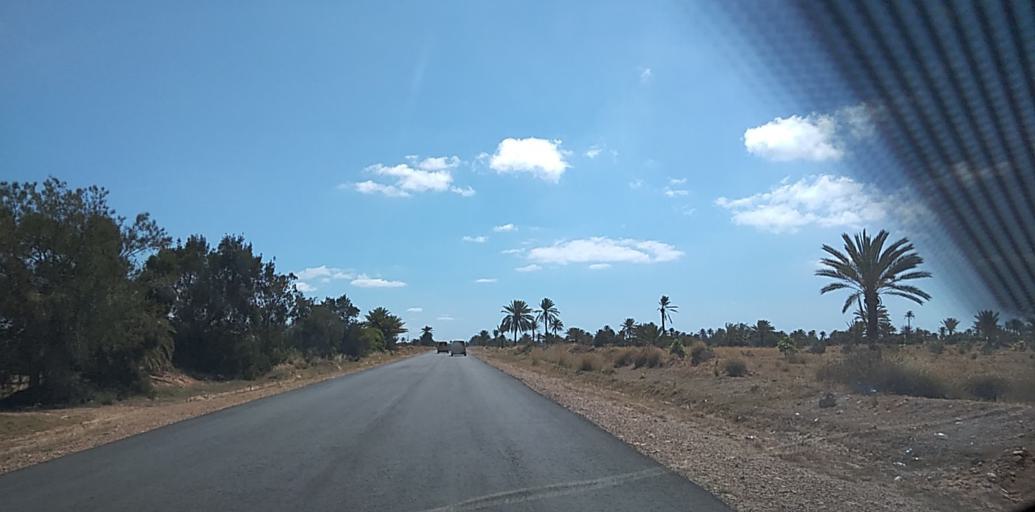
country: TN
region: Safaqis
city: Al Qarmadah
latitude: 34.6573
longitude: 11.0974
